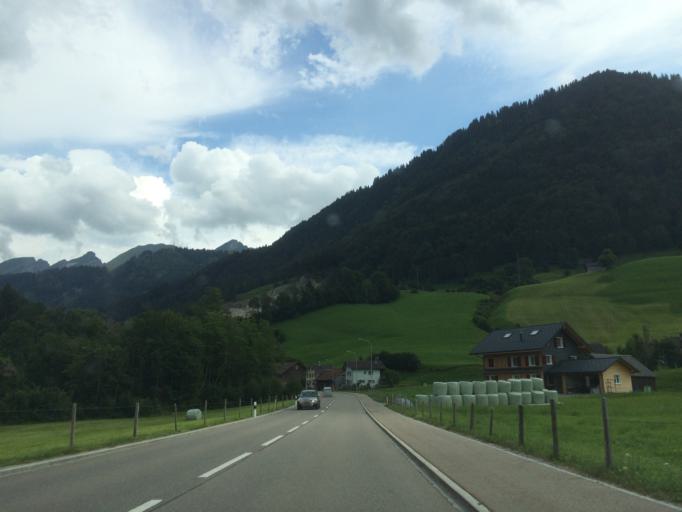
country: CH
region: Saint Gallen
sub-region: Wahlkreis Toggenburg
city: Krummenau
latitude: 47.1950
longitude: 9.2292
